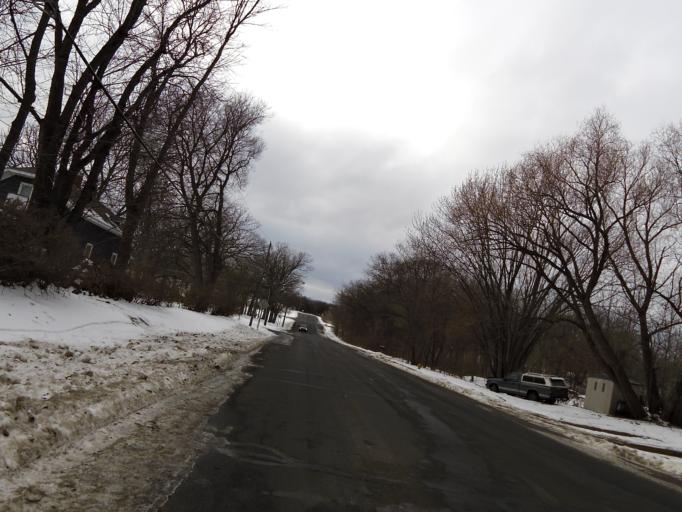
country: US
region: Minnesota
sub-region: Washington County
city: Lakeland
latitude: 44.9605
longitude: -92.7690
